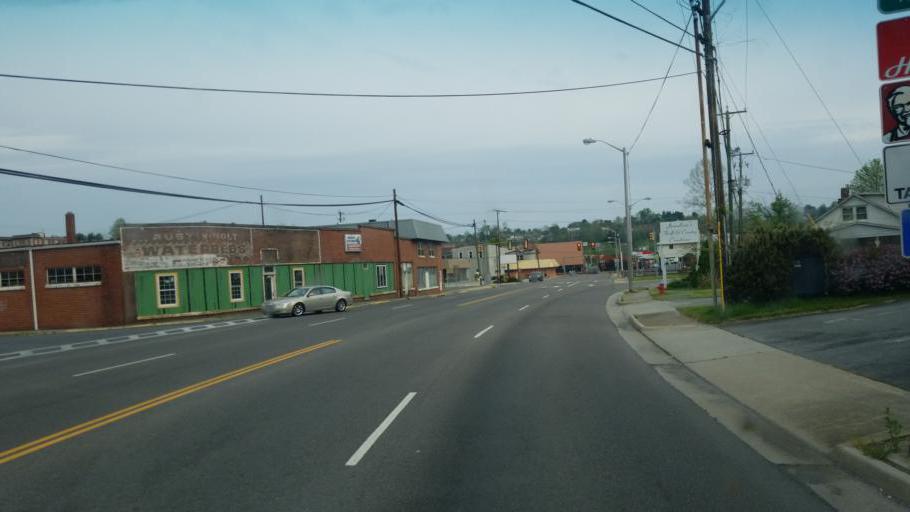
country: US
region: Virginia
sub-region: Smyth County
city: Marion
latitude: 36.8323
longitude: -81.5158
